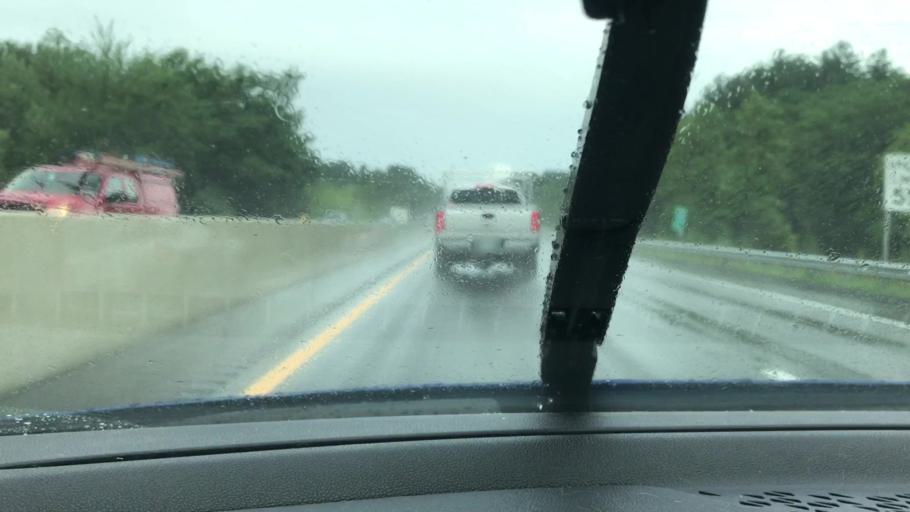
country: US
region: New Hampshire
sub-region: Merrimack County
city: Concord
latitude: 43.2207
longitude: -71.5191
